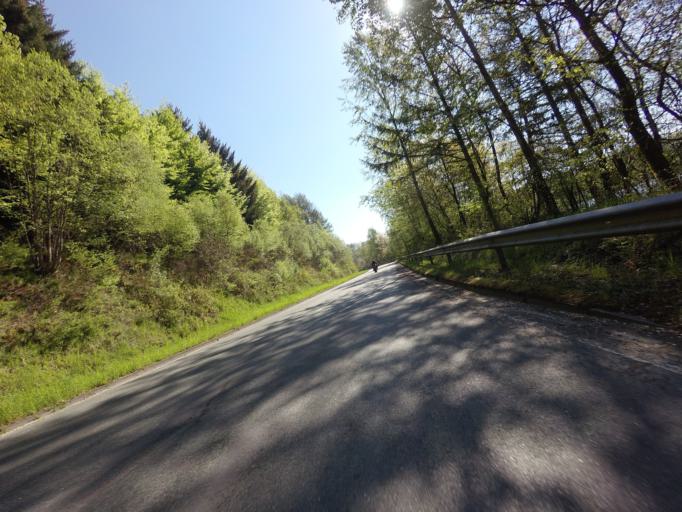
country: DE
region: North Rhine-Westphalia
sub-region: Regierungsbezirk Arnsberg
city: Olpe
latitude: 51.0874
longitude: 7.8221
